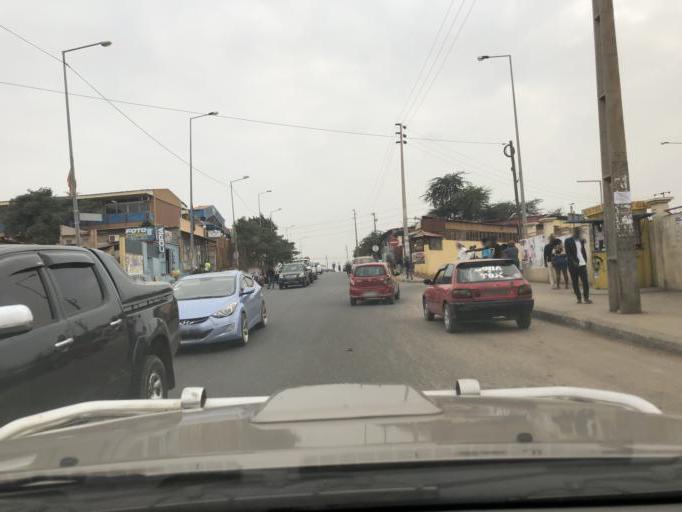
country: AO
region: Luanda
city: Luanda
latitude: -8.9004
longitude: 13.2148
